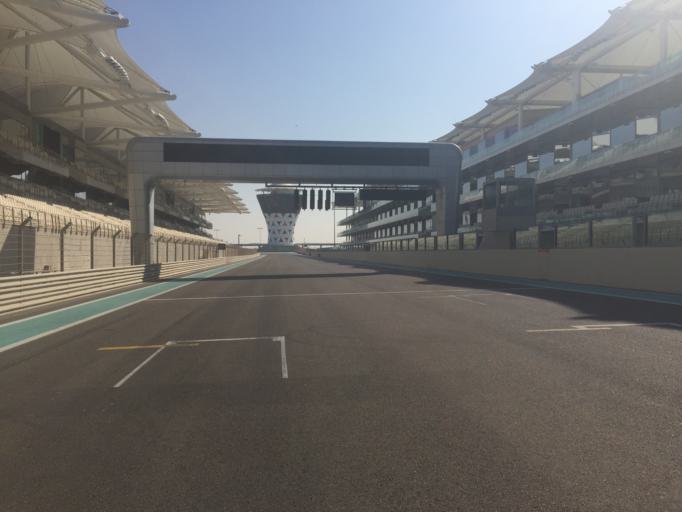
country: AE
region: Abu Dhabi
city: Abu Dhabi
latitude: 24.4699
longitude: 54.6050
